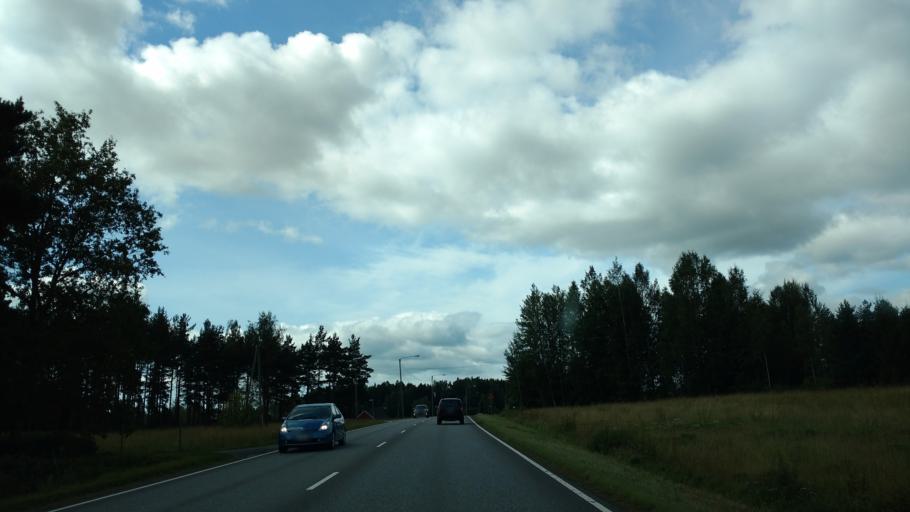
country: FI
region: Varsinais-Suomi
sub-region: Salo
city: Pernioe
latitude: 60.1752
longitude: 23.0359
